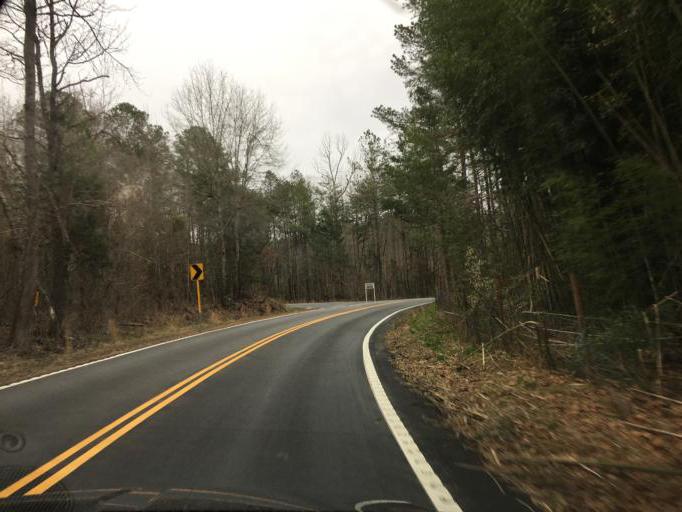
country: US
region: South Carolina
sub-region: Greenville County
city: Travelers Rest
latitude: 34.9382
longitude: -82.5170
